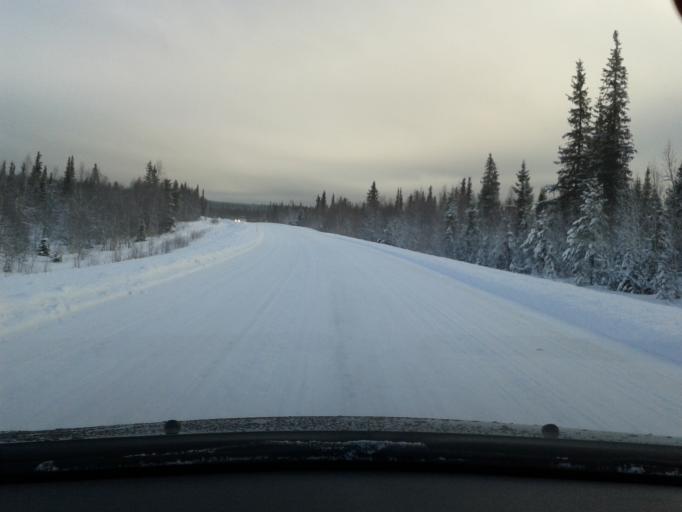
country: SE
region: Vaesterbotten
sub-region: Vilhelmina Kommun
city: Sjoberg
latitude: 65.2570
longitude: 15.7045
